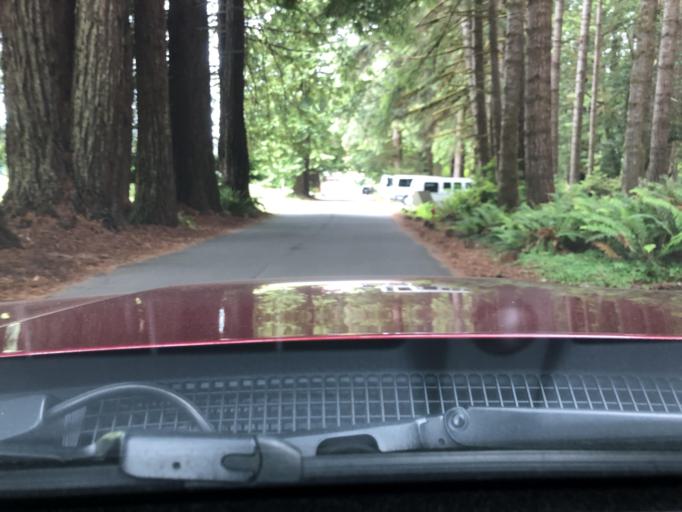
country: US
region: California
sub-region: Humboldt County
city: Westhaven-Moonstone
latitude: 41.3630
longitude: -124.0243
